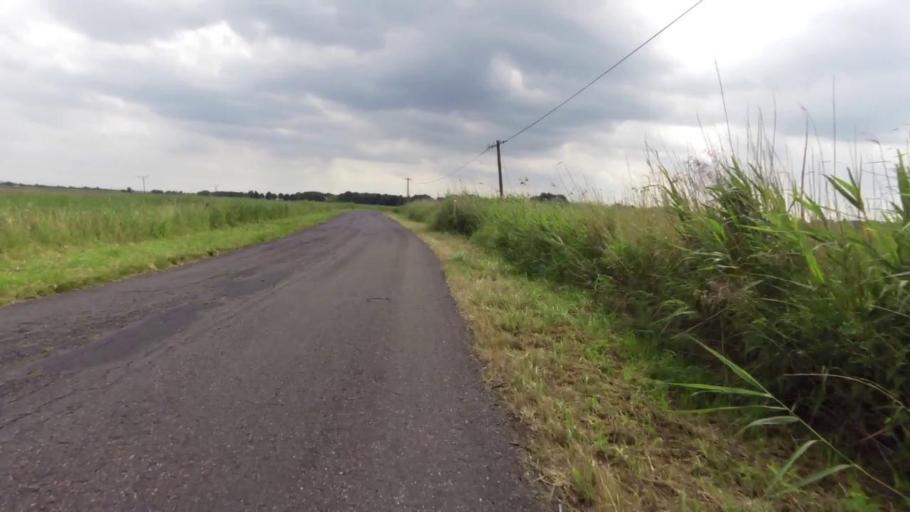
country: PL
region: West Pomeranian Voivodeship
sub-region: Powiat goleniowski
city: Stepnica
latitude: 53.6844
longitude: 14.5494
